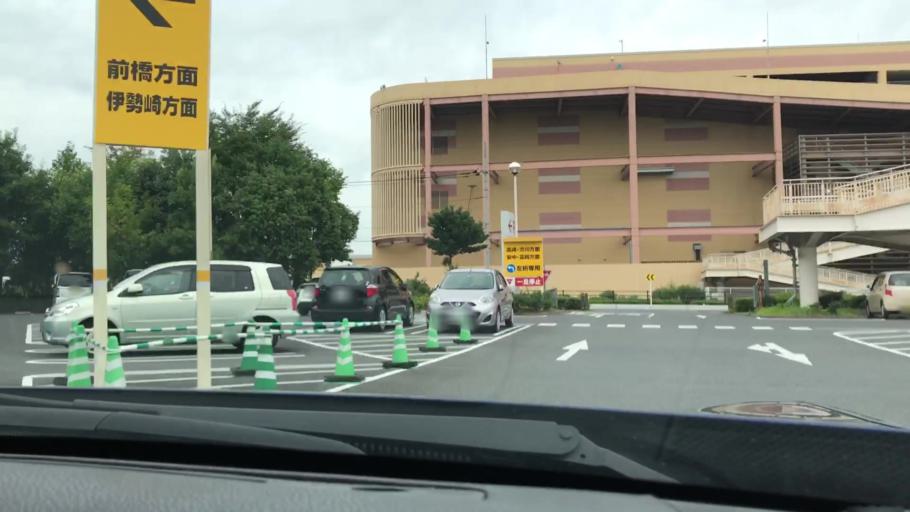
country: JP
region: Gunma
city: Kanekomachi
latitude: 36.3882
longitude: 139.0068
